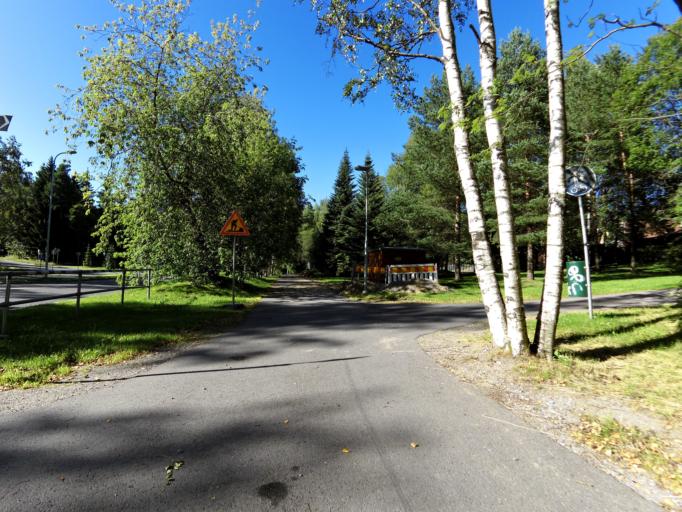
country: FI
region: Pirkanmaa
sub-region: Tampere
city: Pirkkala
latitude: 61.5066
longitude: 23.6286
